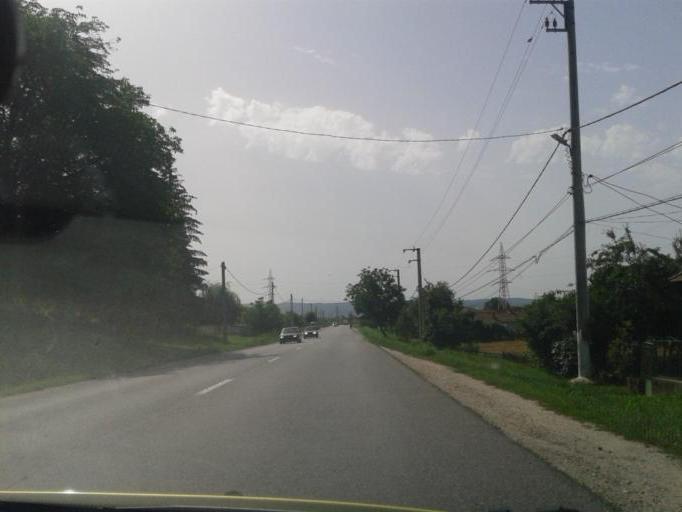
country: RO
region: Valcea
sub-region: Comuna Mihaesti
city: Mihaesti
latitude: 45.0441
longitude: 24.2557
